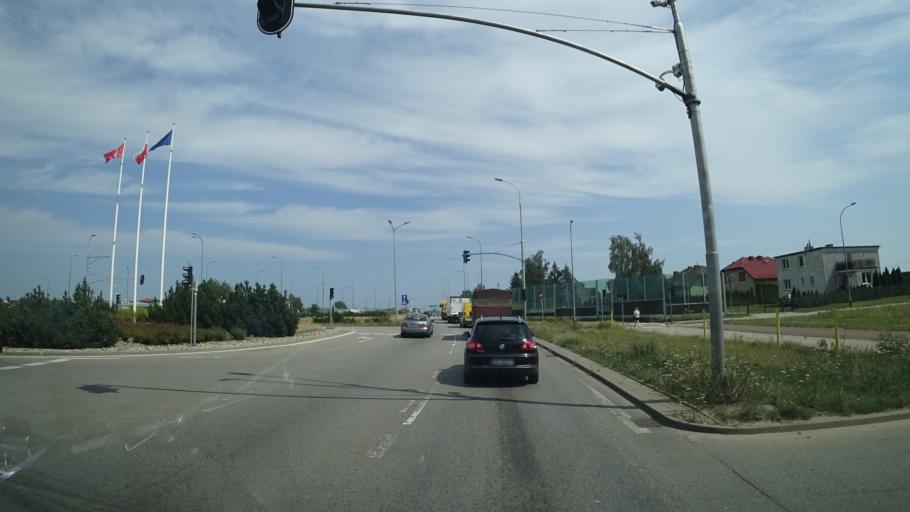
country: PL
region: Pomeranian Voivodeship
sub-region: Powiat gdanski
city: Kowale
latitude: 54.3499
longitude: 18.5106
